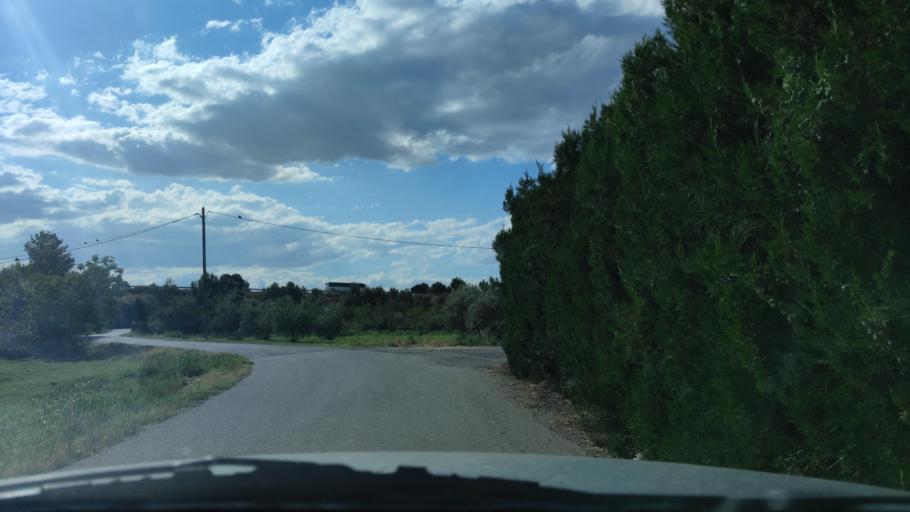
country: ES
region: Catalonia
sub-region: Provincia de Lleida
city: Alpicat
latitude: 41.6281
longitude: 0.5542
